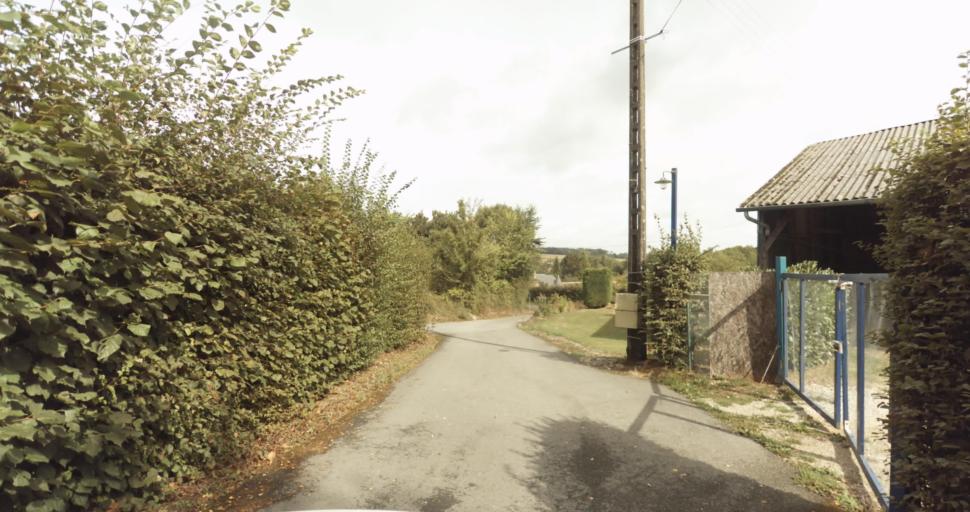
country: FR
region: Lower Normandy
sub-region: Departement de l'Orne
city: Gace
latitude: 48.8309
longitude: 0.3809
